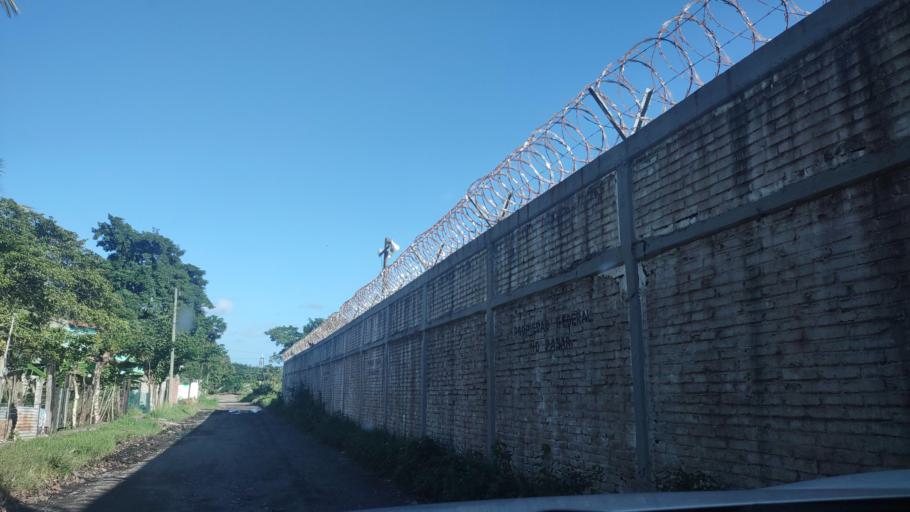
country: MX
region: Veracruz
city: Paso del Toro
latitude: 19.0314
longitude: -96.1367
